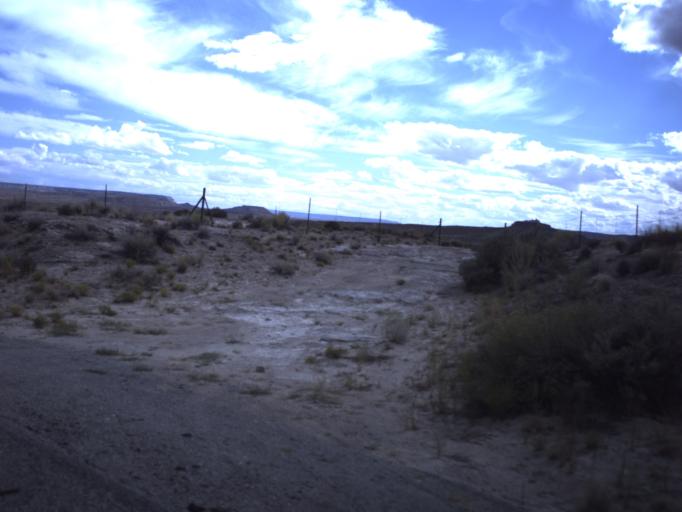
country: US
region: Utah
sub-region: San Juan County
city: Blanding
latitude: 37.2753
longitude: -109.3599
